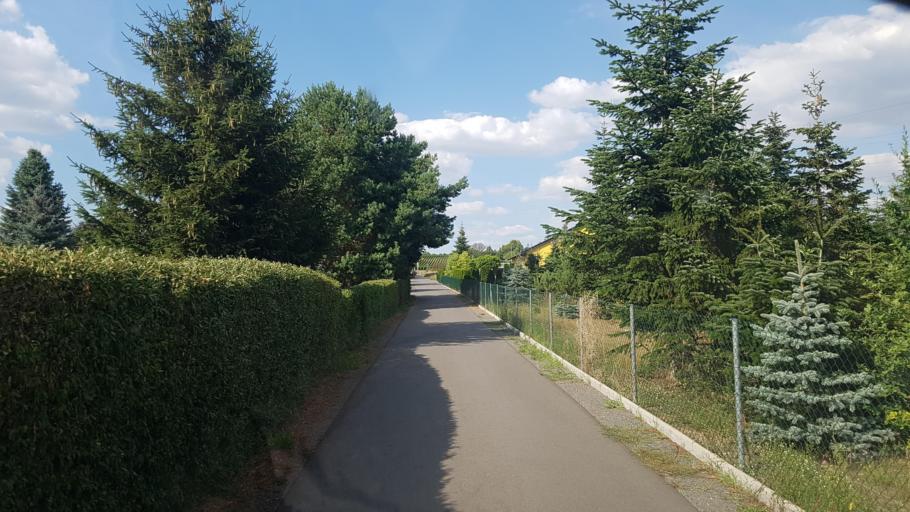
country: DE
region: Saxony-Anhalt
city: Jessen
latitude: 51.7948
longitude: 12.9746
